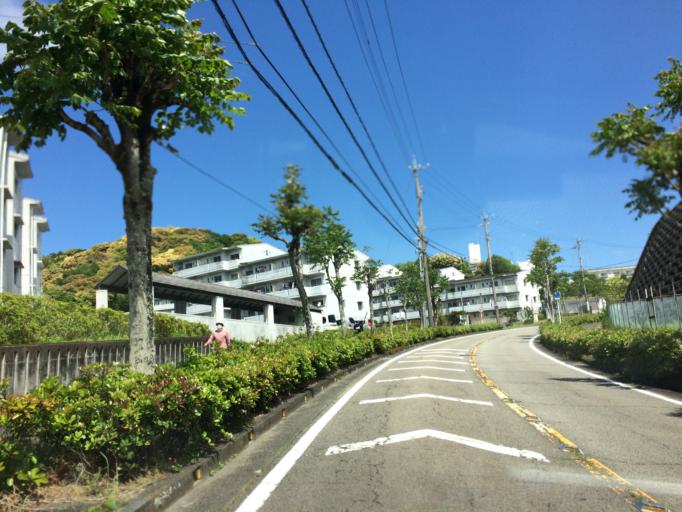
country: JP
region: Shizuoka
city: Fujieda
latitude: 34.8581
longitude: 138.2289
